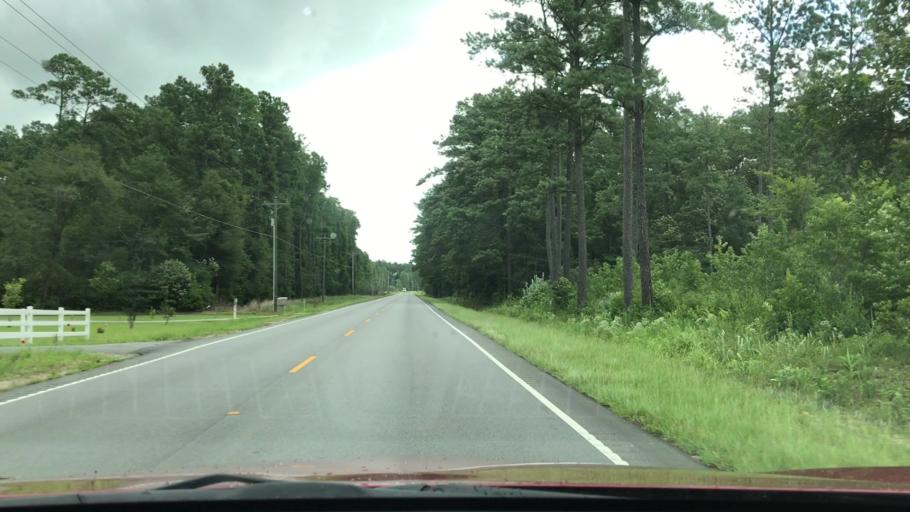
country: US
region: South Carolina
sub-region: Horry County
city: Loris
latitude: 33.9189
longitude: -78.8050
